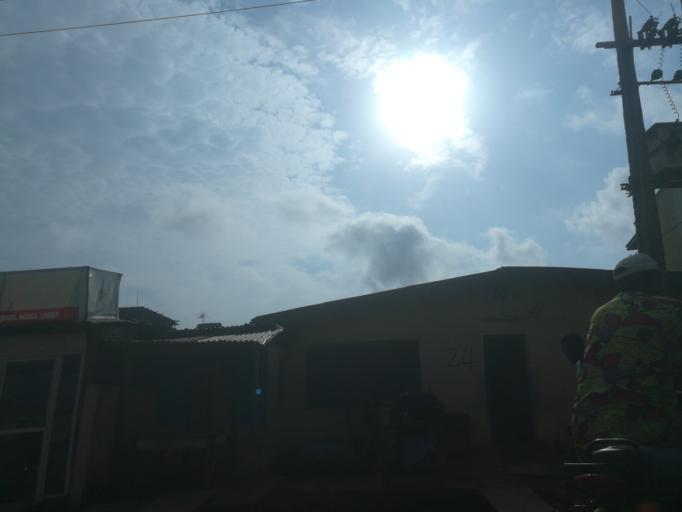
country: NG
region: Lagos
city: Agege
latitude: 6.6226
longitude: 3.3127
